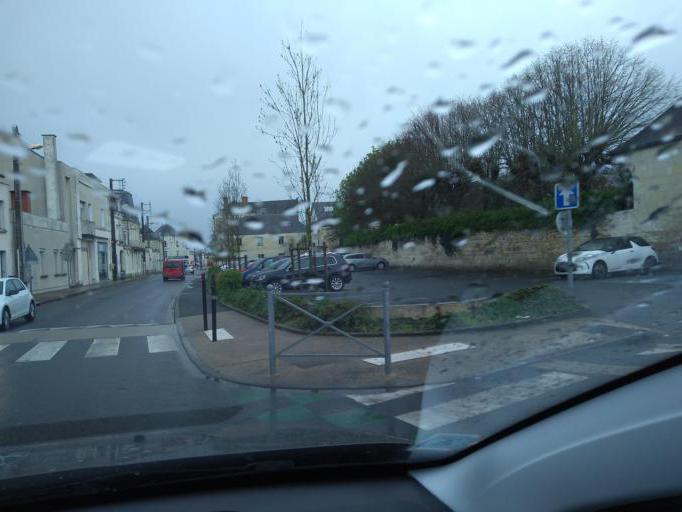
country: FR
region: Poitou-Charentes
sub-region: Departement de la Vienne
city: Loudun
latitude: 47.0103
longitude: 0.0872
